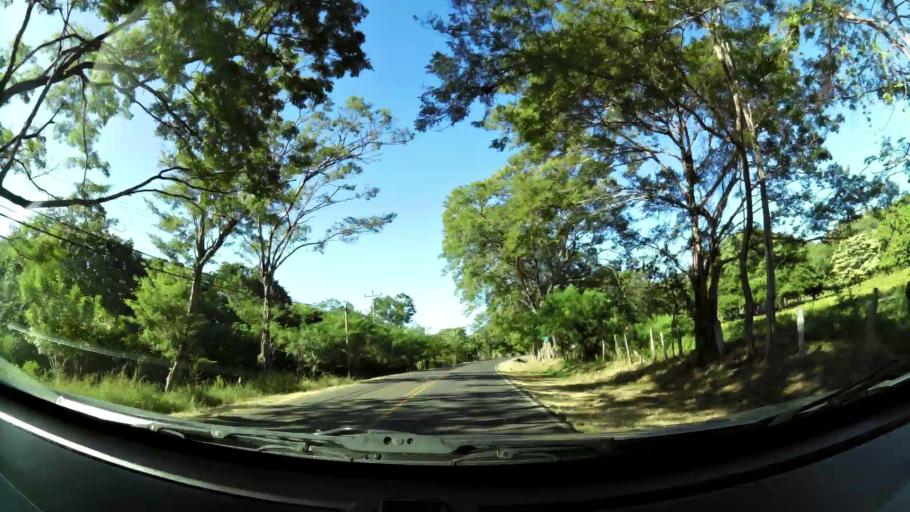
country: CR
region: Guanacaste
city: Belen
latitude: 10.3981
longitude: -85.6062
